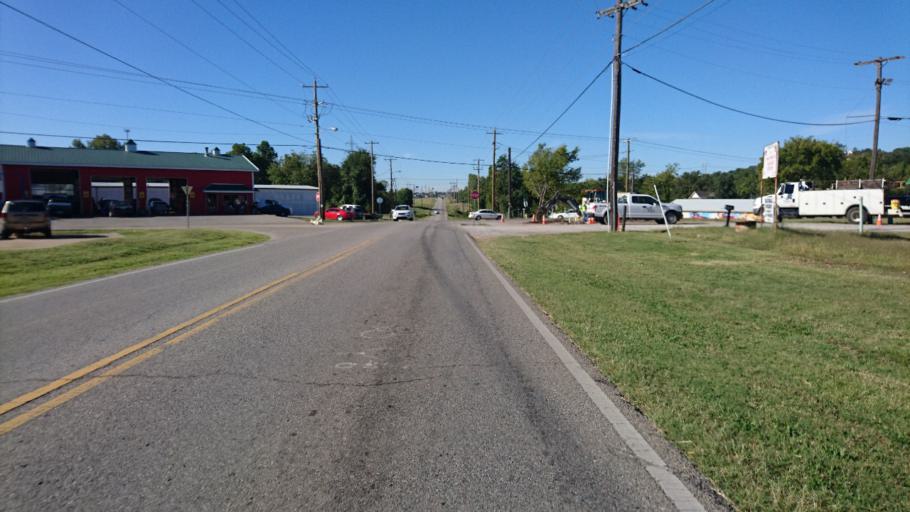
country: US
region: Oklahoma
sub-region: Rogers County
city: Catoosa
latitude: 36.1774
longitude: -95.7518
